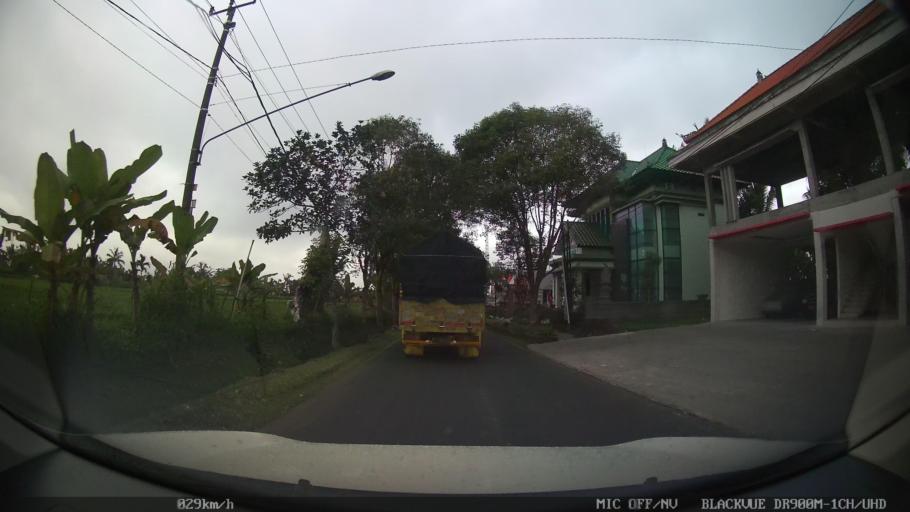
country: ID
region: Bali
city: Banjar Buahan
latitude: -8.4055
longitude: 115.2464
